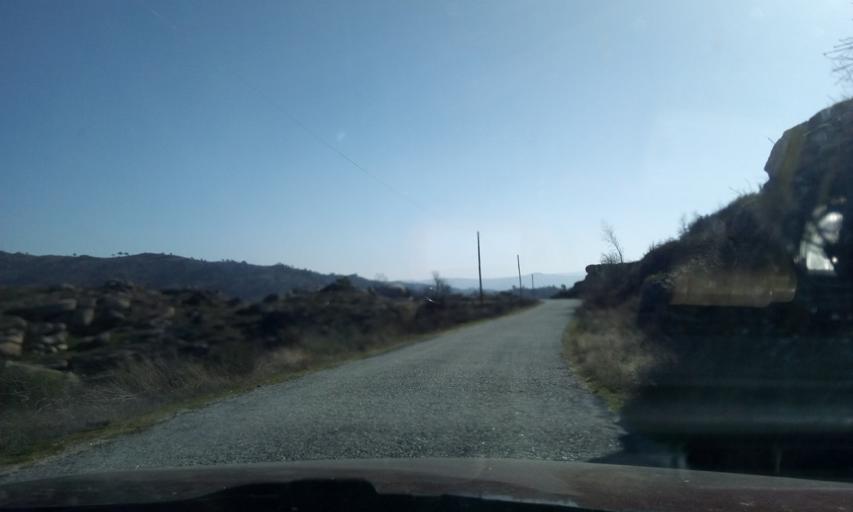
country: PT
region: Guarda
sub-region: Celorico da Beira
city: Celorico da Beira
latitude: 40.6909
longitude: -7.4359
